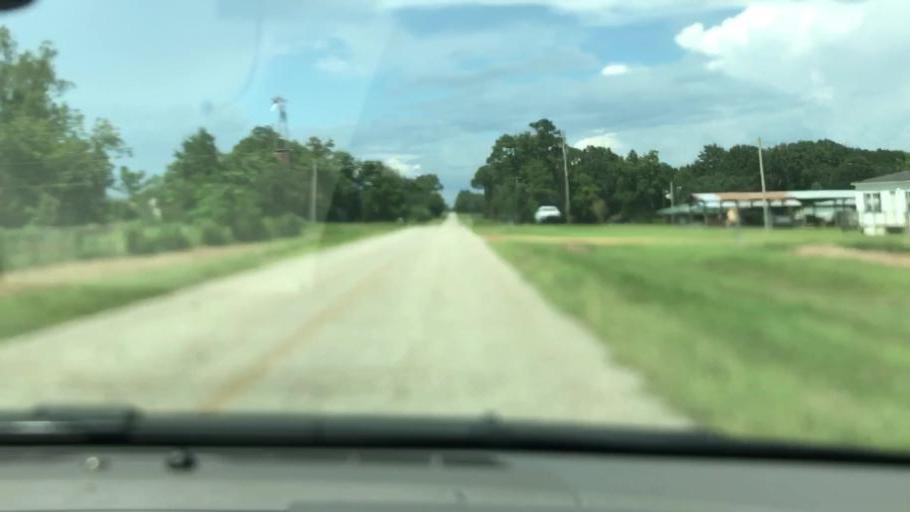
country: US
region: Georgia
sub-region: Early County
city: Blakely
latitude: 31.2018
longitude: -85.0036
